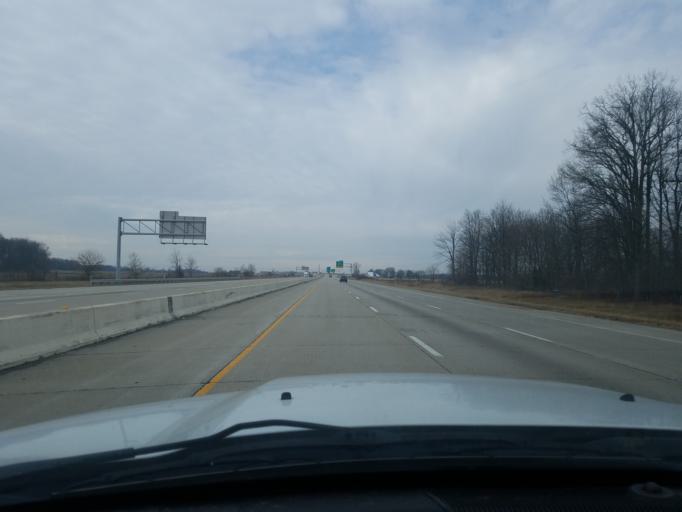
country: US
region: Indiana
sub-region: Huntington County
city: Roanoke
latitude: 40.9553
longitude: -85.2611
